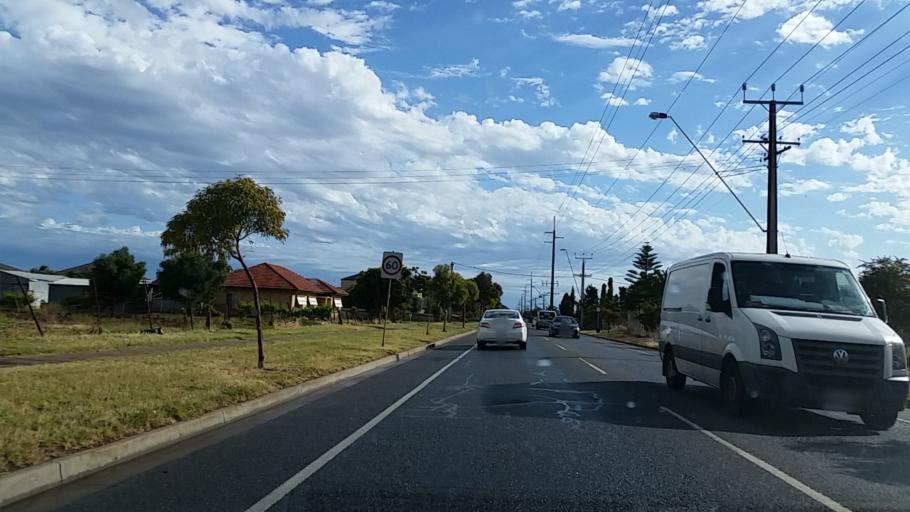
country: AU
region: South Australia
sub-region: Salisbury
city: Salisbury
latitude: -34.7853
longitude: 138.6050
